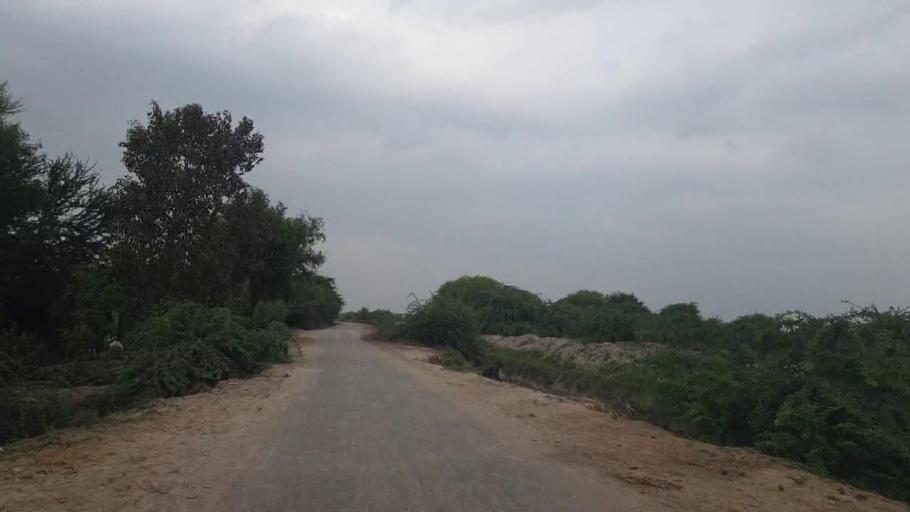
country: PK
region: Sindh
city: Badin
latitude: 24.6243
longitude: 68.6822
